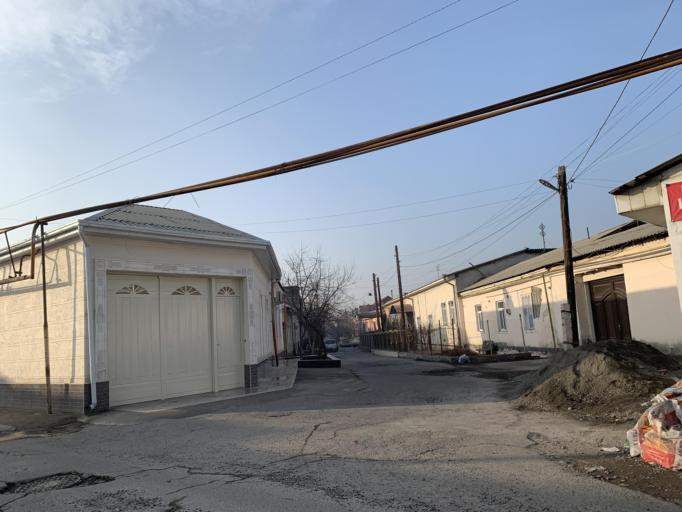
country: UZ
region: Fergana
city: Qo`qon
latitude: 40.5418
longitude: 70.9315
